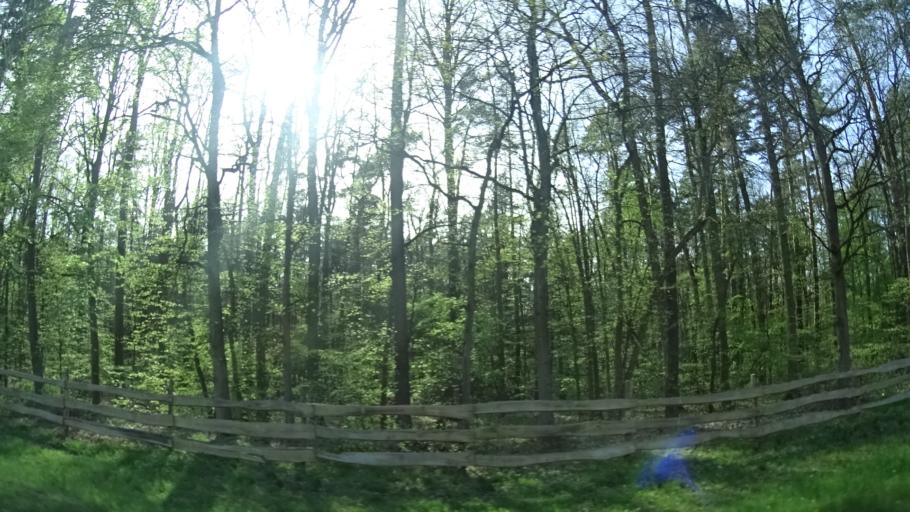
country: DE
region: Bavaria
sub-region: Regierungsbezirk Unterfranken
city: Schwebheim
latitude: 50.0026
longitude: 10.2386
